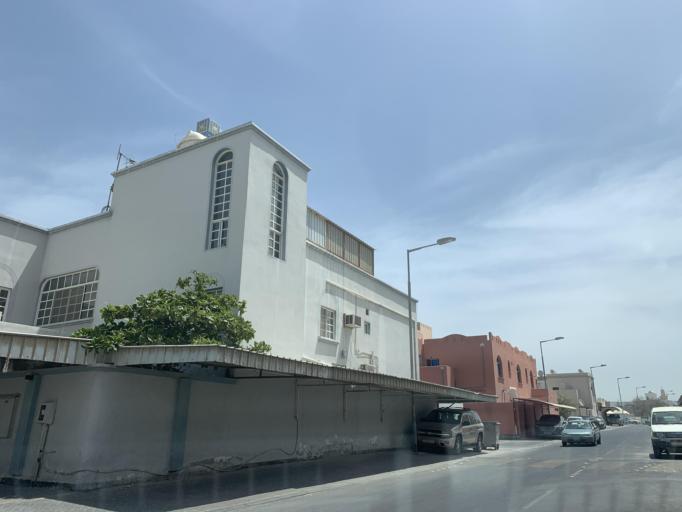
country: BH
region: Northern
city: Ar Rifa'
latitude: 26.1415
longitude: 50.5627
